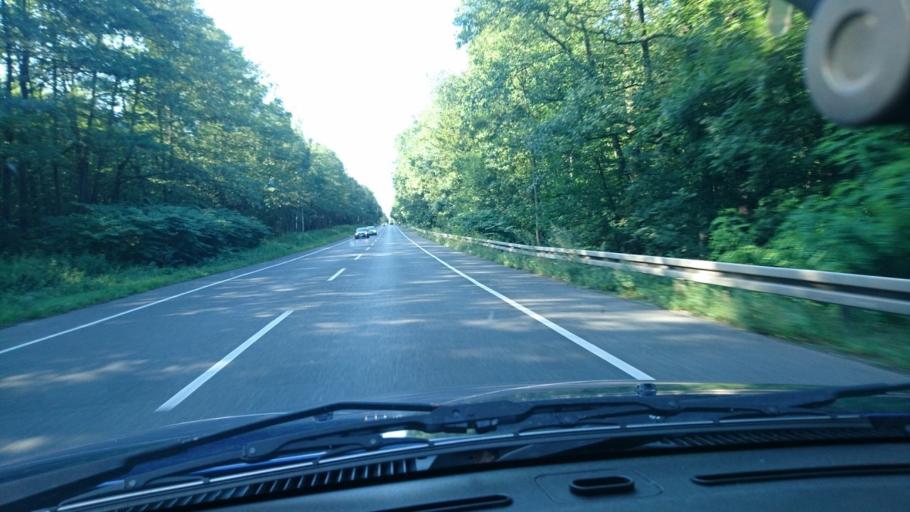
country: PL
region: Silesian Voivodeship
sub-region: Gliwice
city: Gliwice
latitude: 50.3330
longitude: 18.6569
